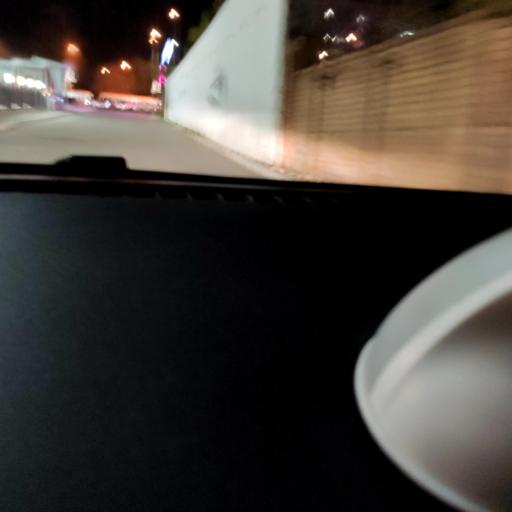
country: RU
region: Samara
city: Samara
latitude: 53.2196
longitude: 50.1533
